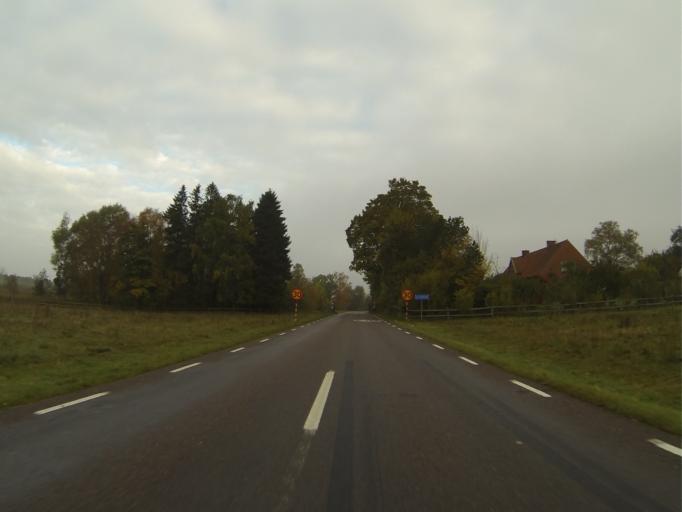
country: SE
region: Skane
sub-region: Lunds Kommun
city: Veberod
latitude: 55.6817
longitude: 13.4982
